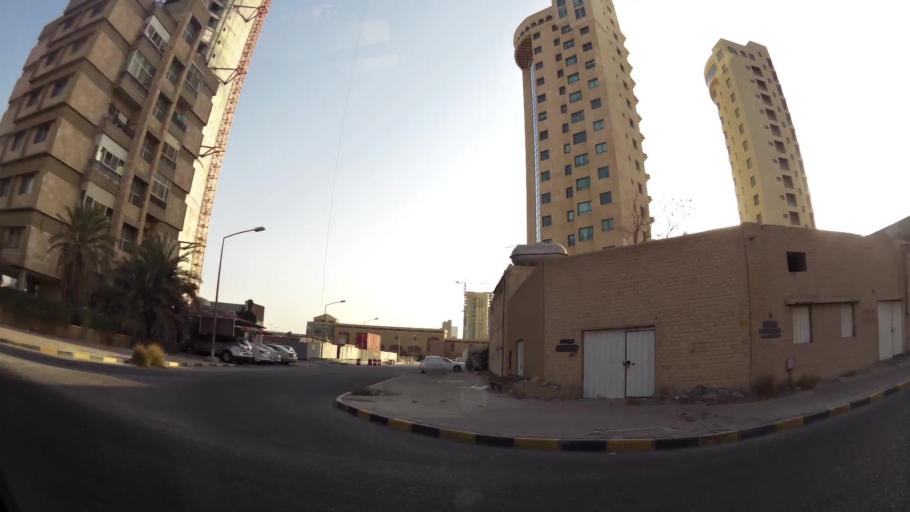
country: KW
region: Muhafazat Hawalli
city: As Salimiyah
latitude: 29.3391
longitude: 48.0627
